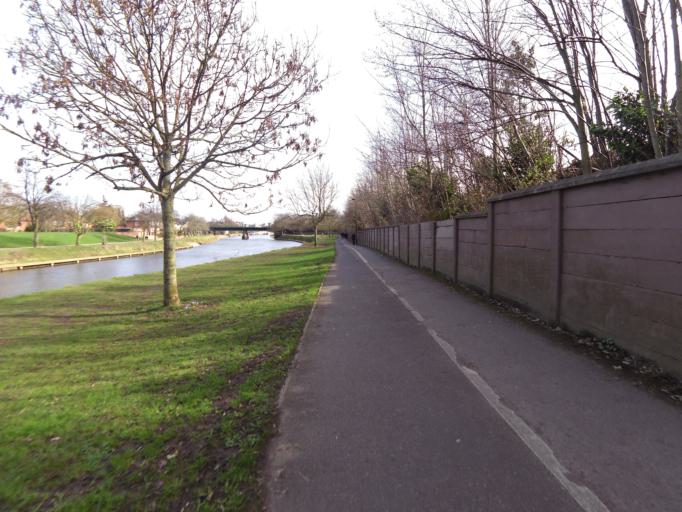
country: GB
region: England
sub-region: City of York
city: York
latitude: 53.9619
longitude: -1.0967
